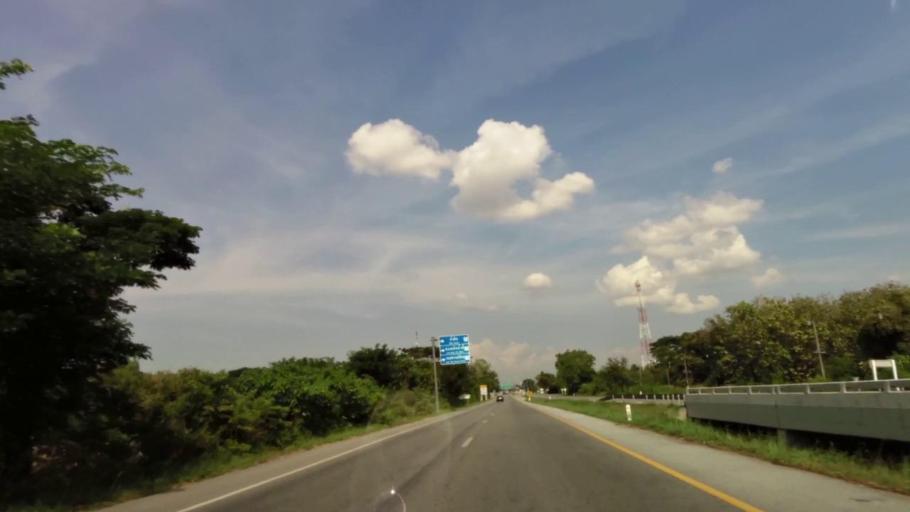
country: TH
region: Uttaradit
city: Thong Saen Khan
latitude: 17.4650
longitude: 100.2370
